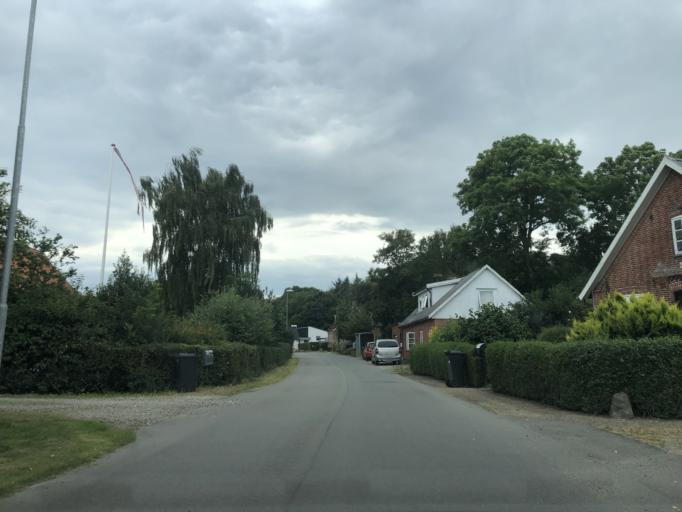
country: DK
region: Central Jutland
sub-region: Skanderborg Kommune
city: Ry
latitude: 56.1505
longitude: 9.7844
